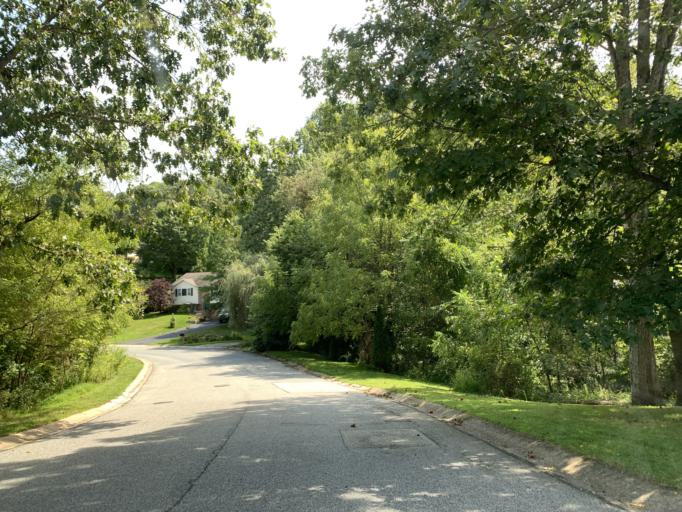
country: US
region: Pennsylvania
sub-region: York County
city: Spry
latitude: 39.9043
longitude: -76.6901
